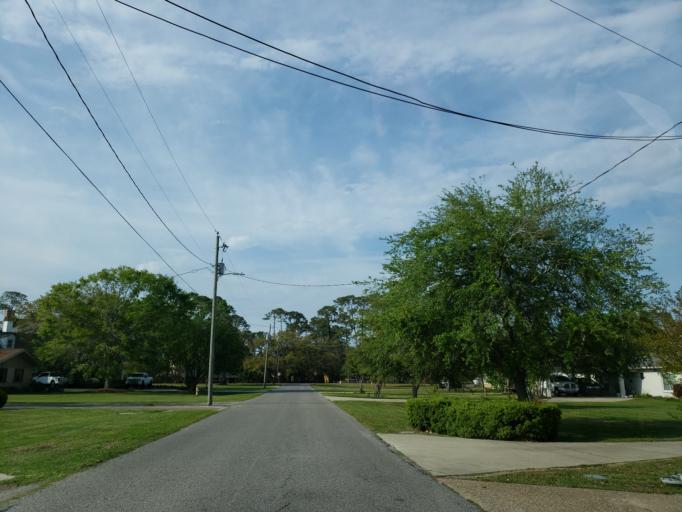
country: US
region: Mississippi
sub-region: Harrison County
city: West Gulfport
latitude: 30.4107
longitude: -89.0481
